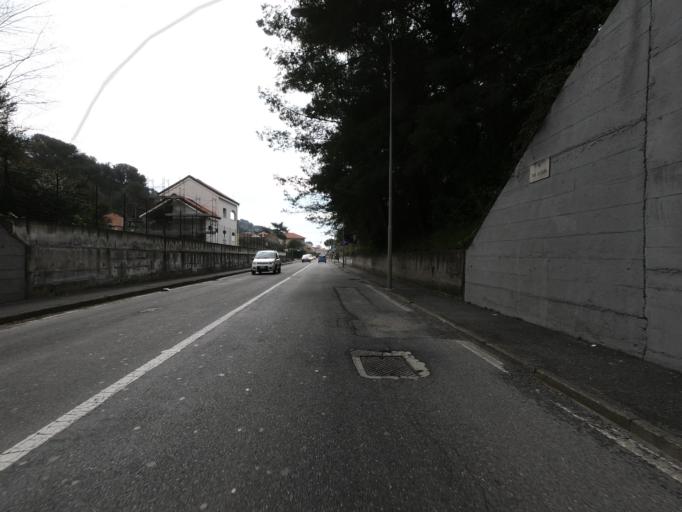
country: IT
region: Liguria
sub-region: Provincia di Savona
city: Andora
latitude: 43.9620
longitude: 8.1427
